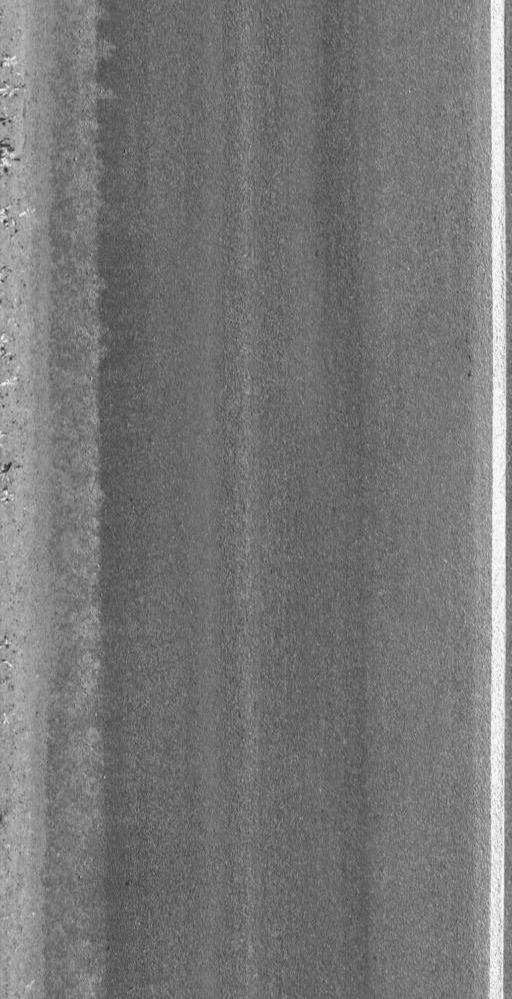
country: US
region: Vermont
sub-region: Washington County
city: Waterbury
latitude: 44.4200
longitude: -72.8524
